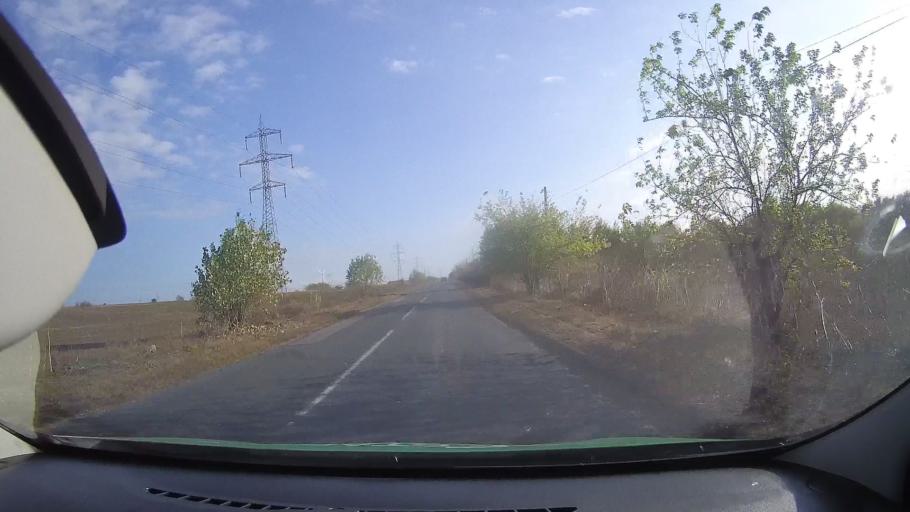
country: RO
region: Constanta
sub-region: Comuna Corbu
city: Corbu
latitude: 44.3732
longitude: 28.6651
